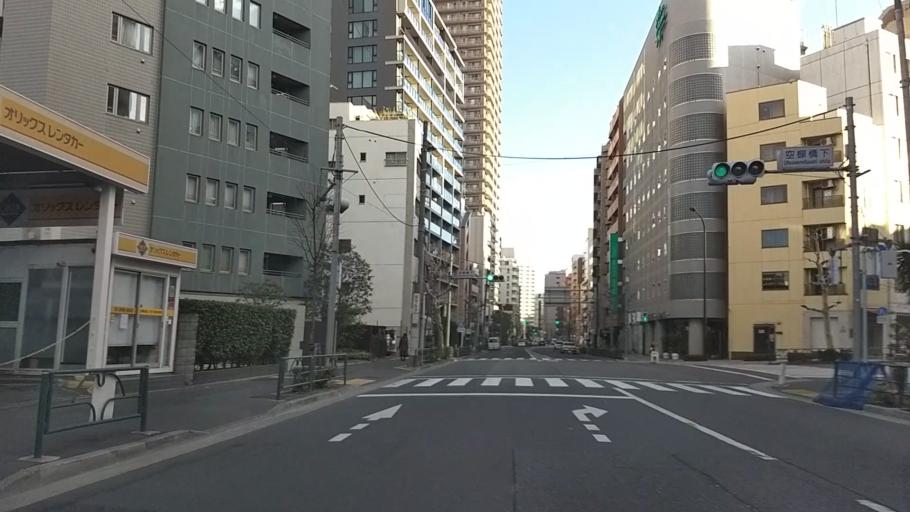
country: JP
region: Tokyo
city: Tokyo
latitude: 35.7354
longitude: 139.7267
